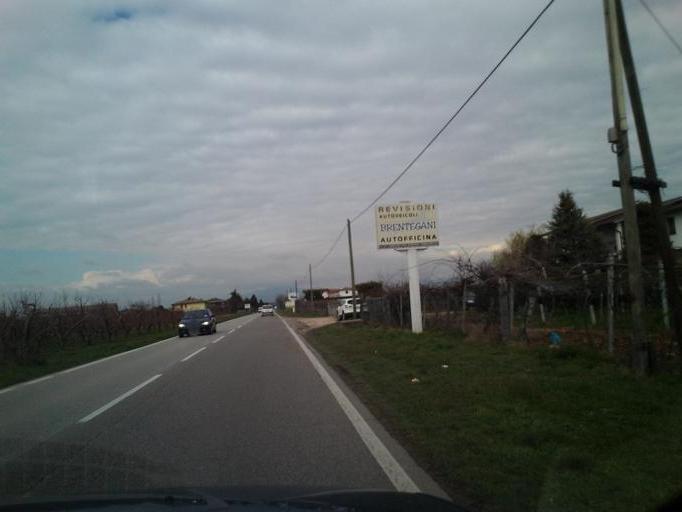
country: IT
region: Veneto
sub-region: Provincia di Verona
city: Villafranca di Verona
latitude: 45.3755
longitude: 10.8461
